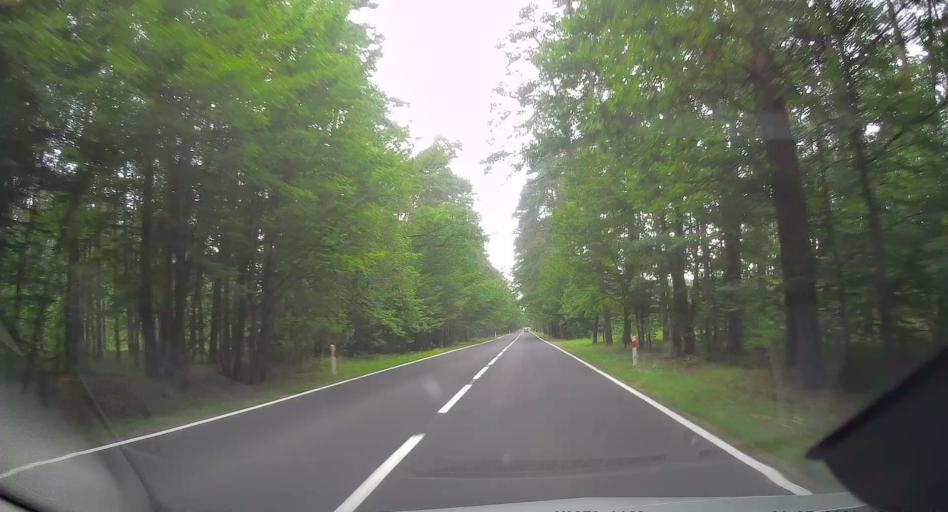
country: PL
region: Lodz Voivodeship
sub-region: Powiat tomaszowski
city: Inowlodz
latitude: 51.5313
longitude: 20.1696
